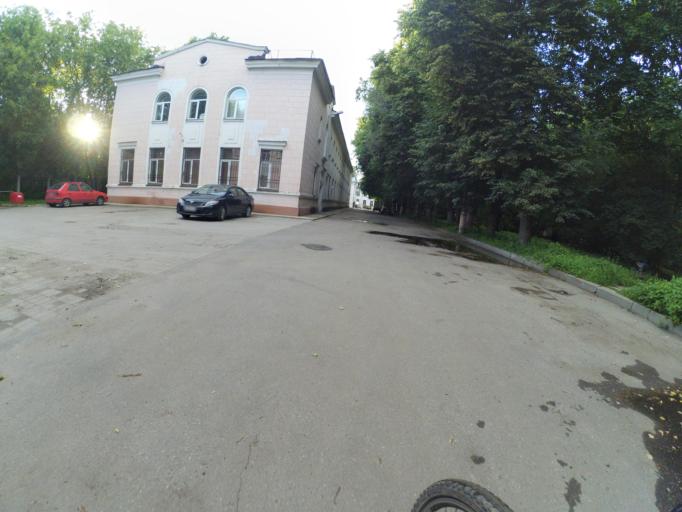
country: RU
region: Moscow
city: Strogino
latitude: 55.8334
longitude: 37.4265
